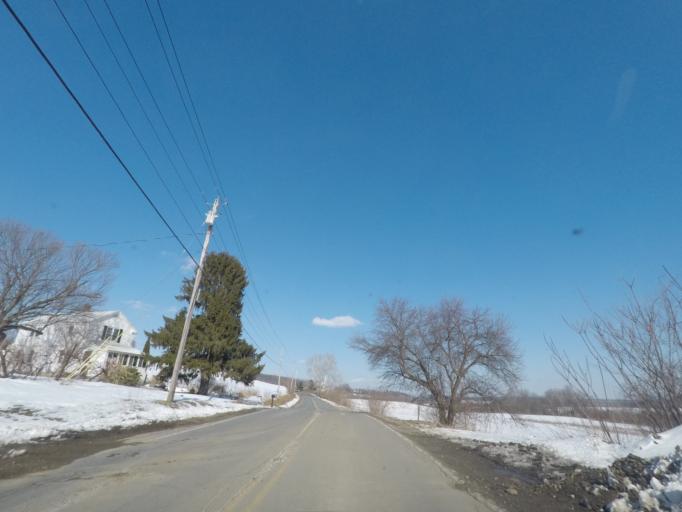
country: US
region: New York
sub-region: Saratoga County
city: Stillwater
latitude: 42.9105
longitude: -73.5653
